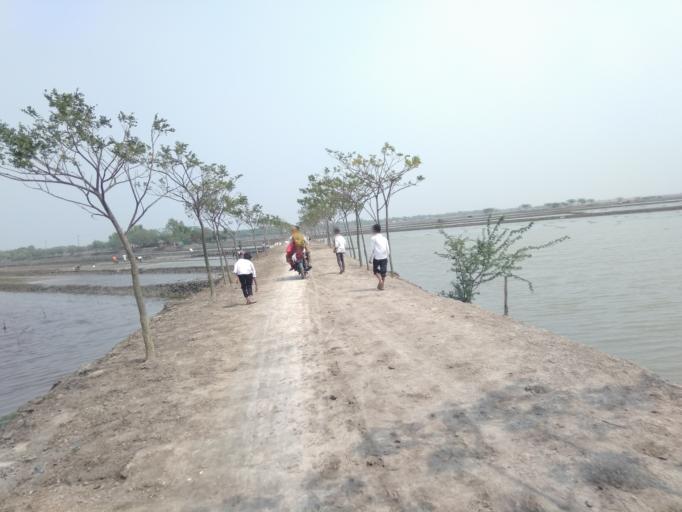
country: IN
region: West Bengal
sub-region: North 24 Parganas
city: Taki
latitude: 22.2741
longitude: 89.2832
